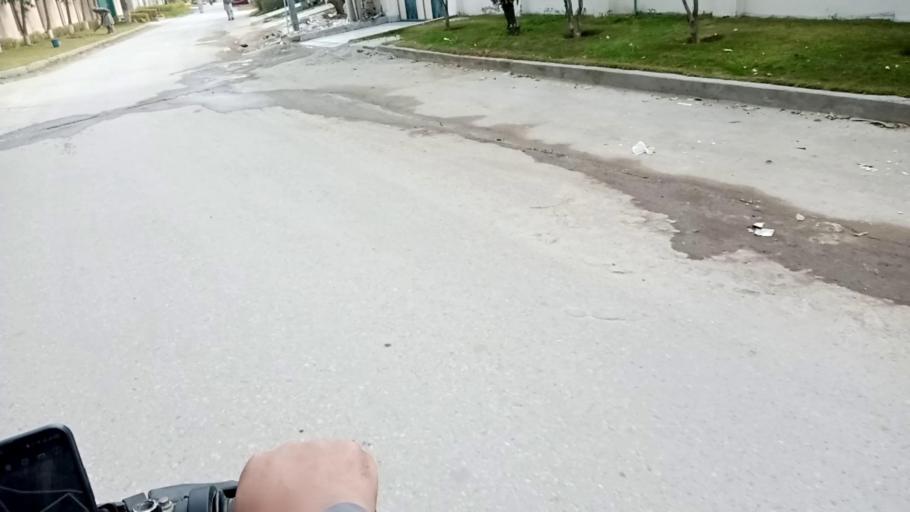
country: PK
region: Khyber Pakhtunkhwa
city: Peshawar
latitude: 33.9640
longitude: 71.4331
